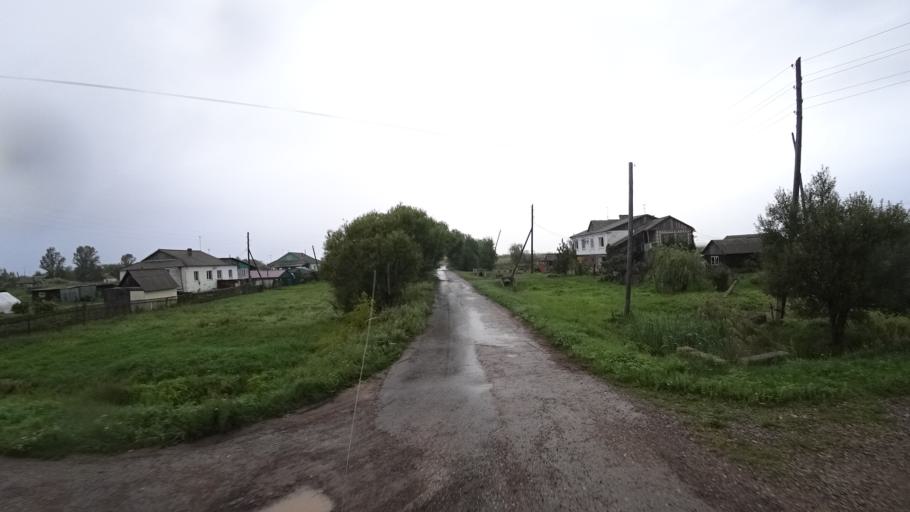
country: RU
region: Primorskiy
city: Chernigovka
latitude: 44.4078
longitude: 132.5324
